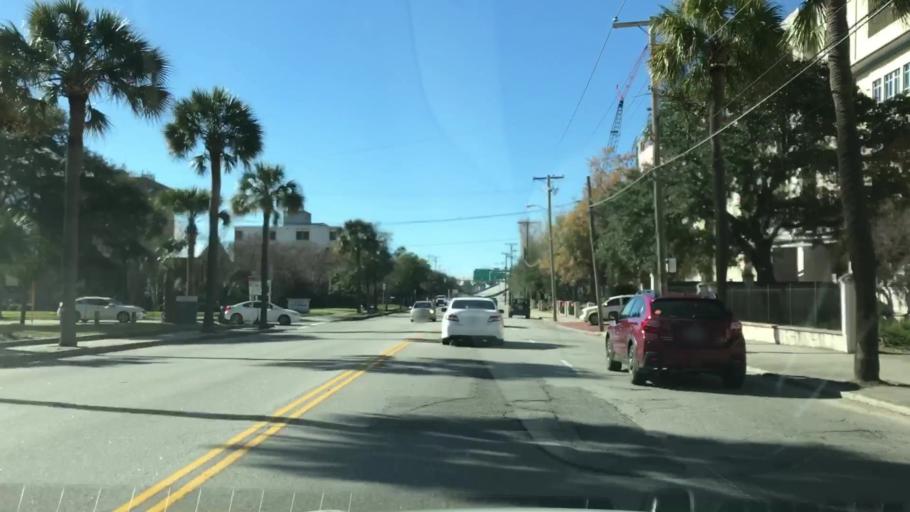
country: US
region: South Carolina
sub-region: Charleston County
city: Charleston
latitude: 32.7825
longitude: -79.9483
